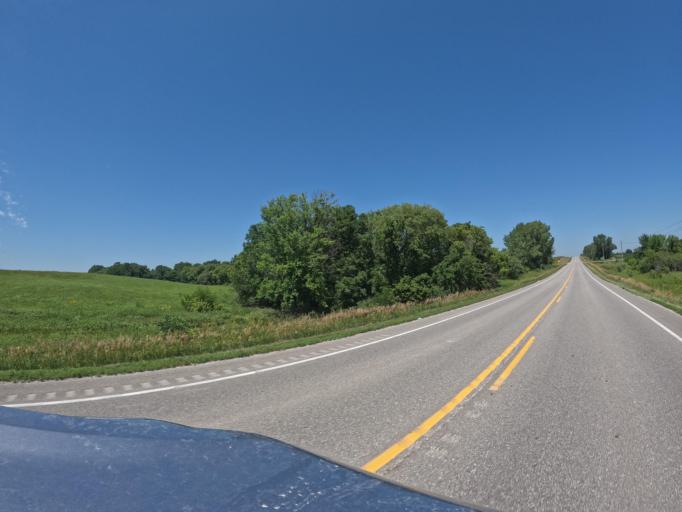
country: US
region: Iowa
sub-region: Keokuk County
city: Sigourney
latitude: 41.4646
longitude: -92.3552
